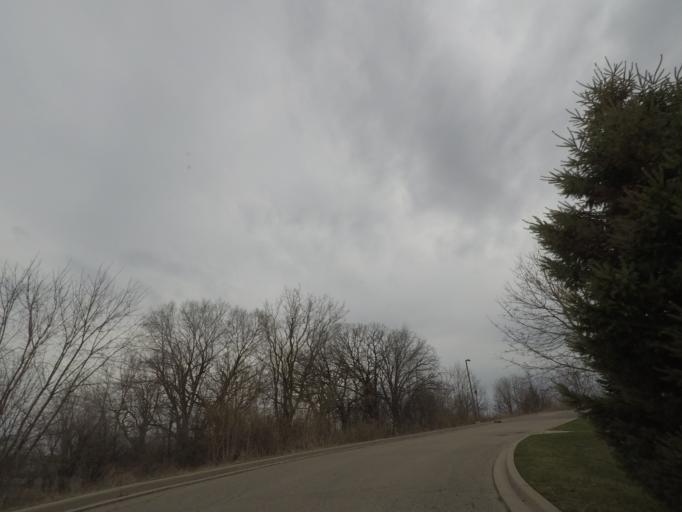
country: US
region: Wisconsin
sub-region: Dane County
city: Middleton
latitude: 43.1074
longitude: -89.5368
